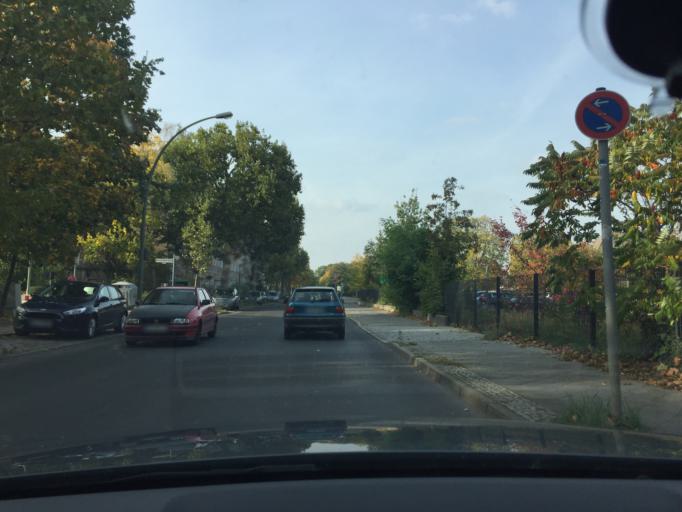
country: DE
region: Berlin
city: Buch
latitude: 52.6294
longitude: 13.5058
